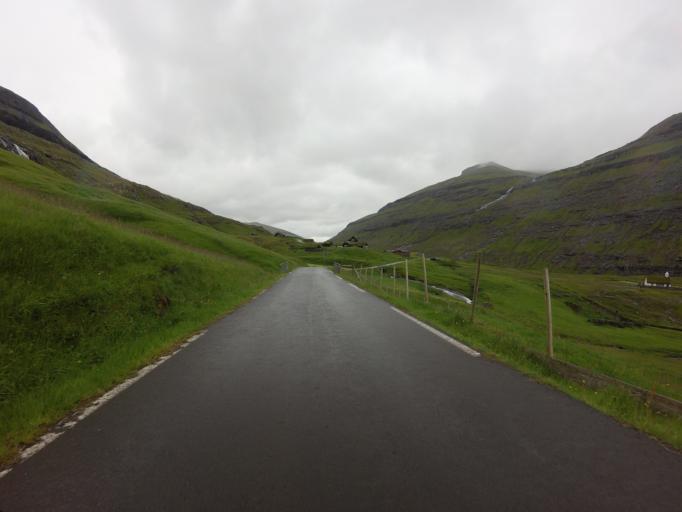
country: FO
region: Streymoy
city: Vestmanna
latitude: 62.2480
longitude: -7.1788
